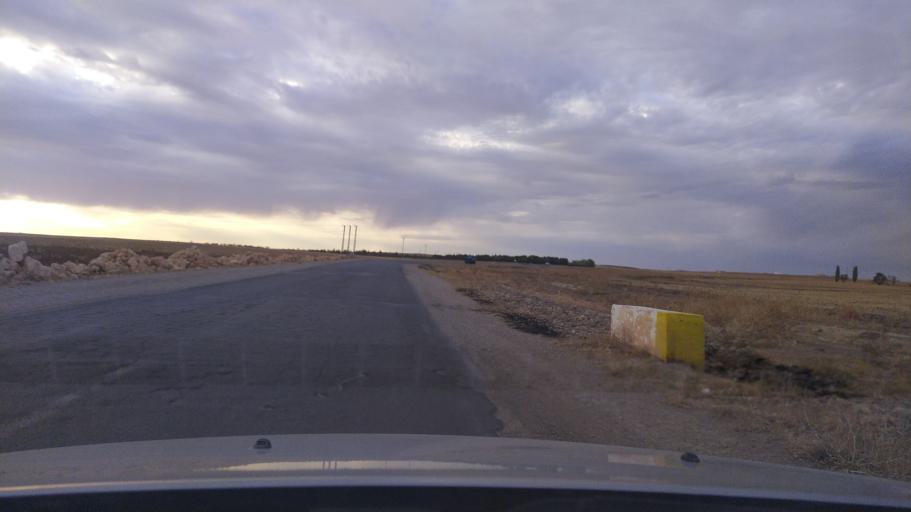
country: DZ
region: Tiaret
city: Frenda
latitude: 34.9814
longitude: 1.1464
